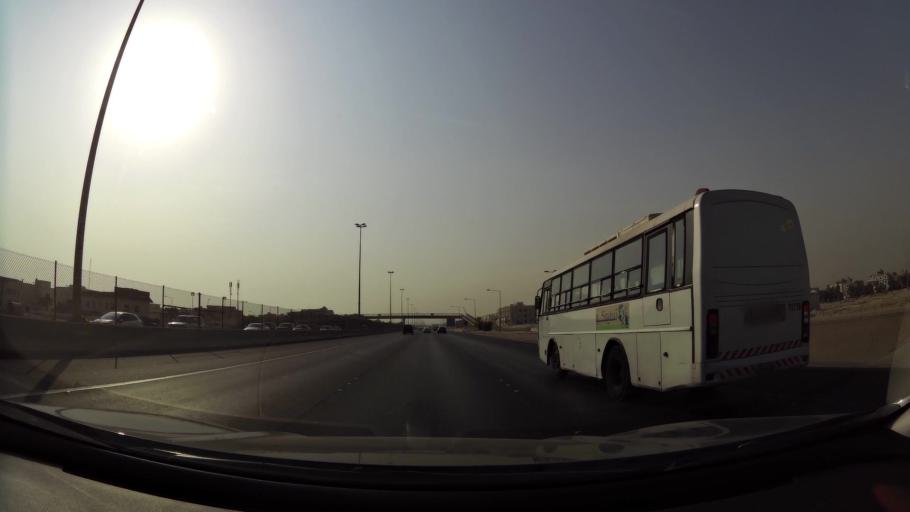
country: KW
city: Al Funaytis
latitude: 29.2283
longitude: 48.0982
